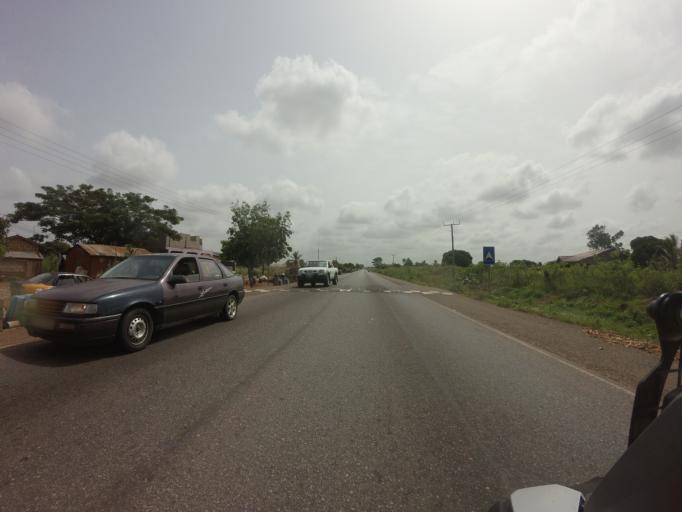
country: GH
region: Volta
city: Anloga
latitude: 5.8932
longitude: 0.4958
